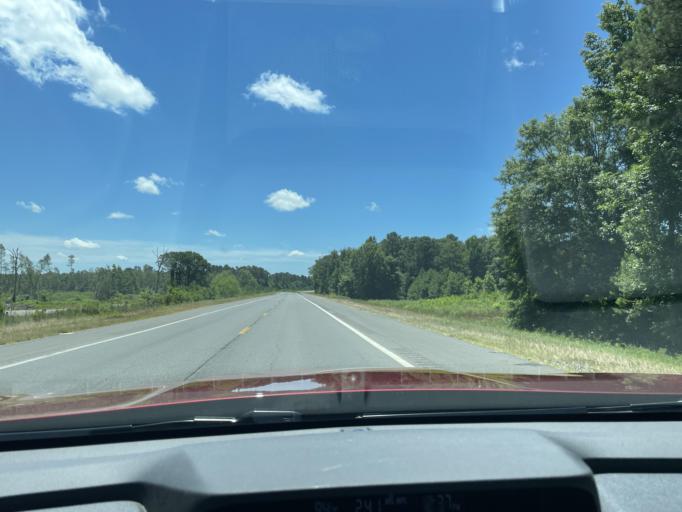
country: US
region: Arkansas
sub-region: Jefferson County
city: Pine Bluff
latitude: 34.1374
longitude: -91.9735
